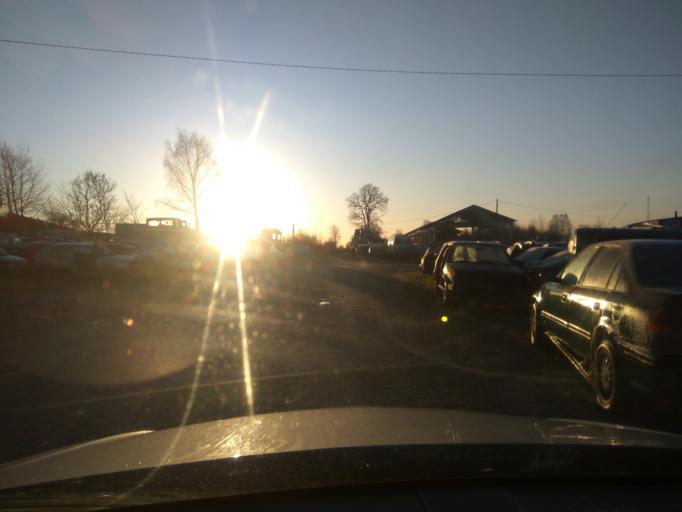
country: LV
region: Kuldigas Rajons
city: Kuldiga
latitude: 56.9599
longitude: 22.0096
